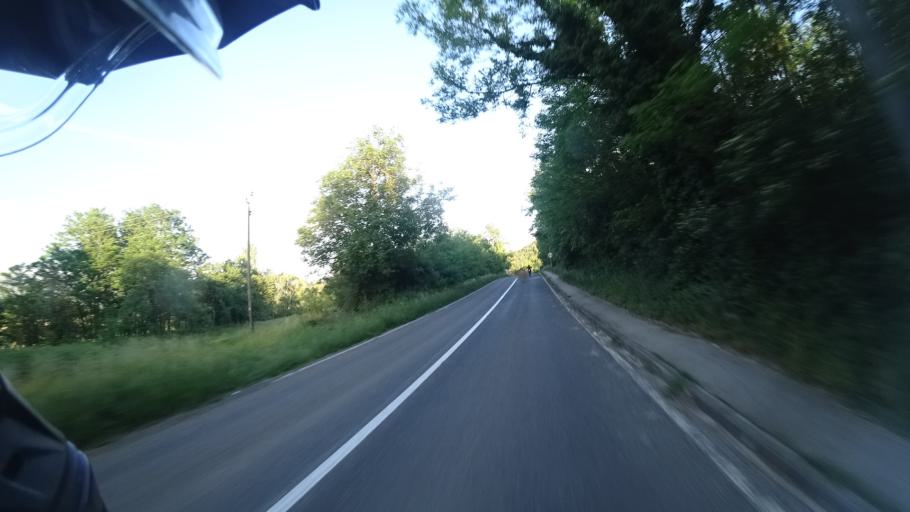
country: HR
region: Sibensko-Kniniska
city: Knin
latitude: 43.9050
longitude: 16.4064
